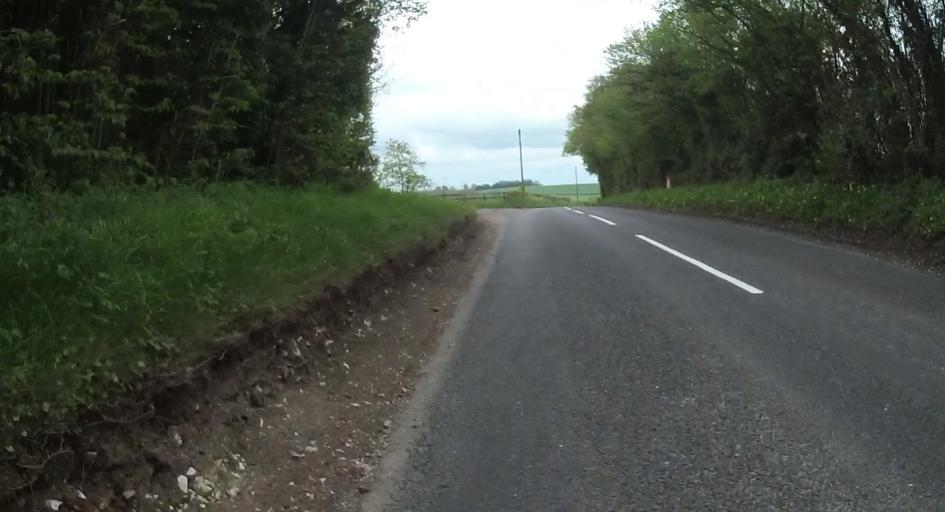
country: GB
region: England
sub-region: Hampshire
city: Colden Common
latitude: 51.0241
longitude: -1.2646
